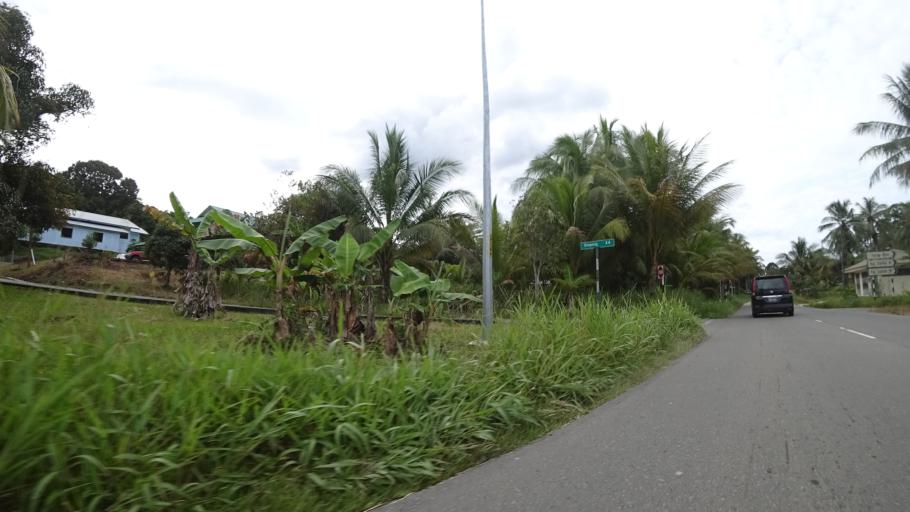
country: BN
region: Brunei and Muara
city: Bandar Seri Begawan
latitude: 4.8687
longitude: 114.9417
